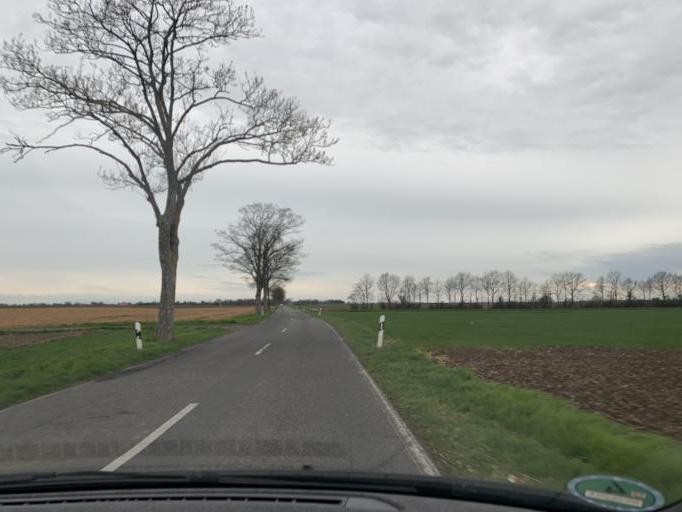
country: DE
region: North Rhine-Westphalia
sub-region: Regierungsbezirk Koln
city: Norvenich
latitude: 50.8019
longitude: 6.7145
